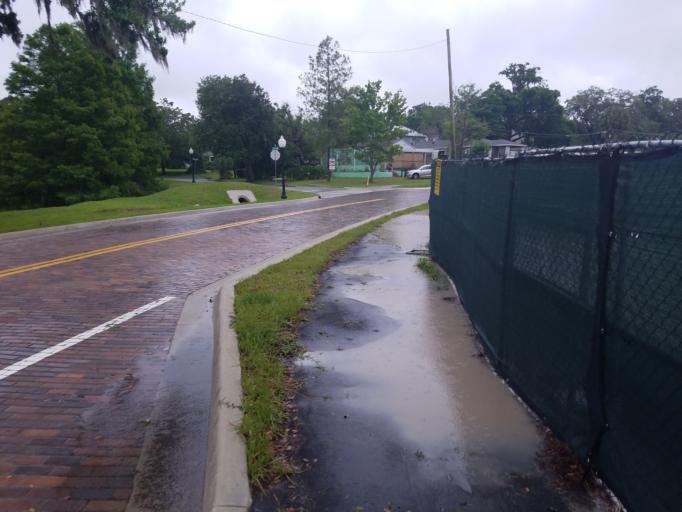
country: US
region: Florida
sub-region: Orange County
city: Orlando
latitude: 28.5669
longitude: -81.3717
